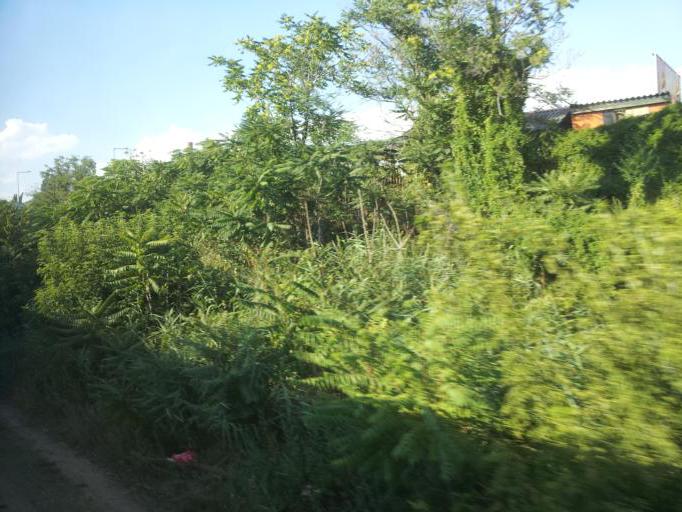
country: HU
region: Budapest
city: Budapest XX. keruelet
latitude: 47.4218
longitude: 19.1053
